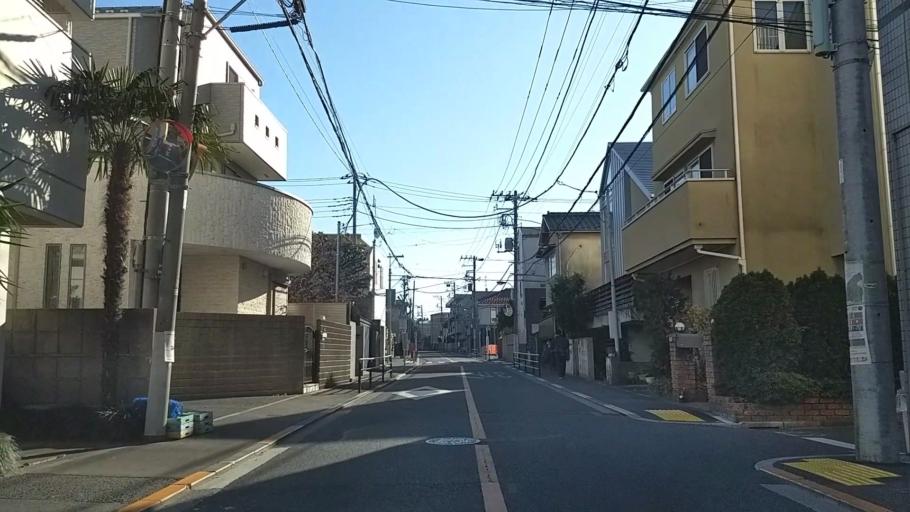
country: JP
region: Tokyo
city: Tokyo
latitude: 35.7149
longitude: 139.7332
